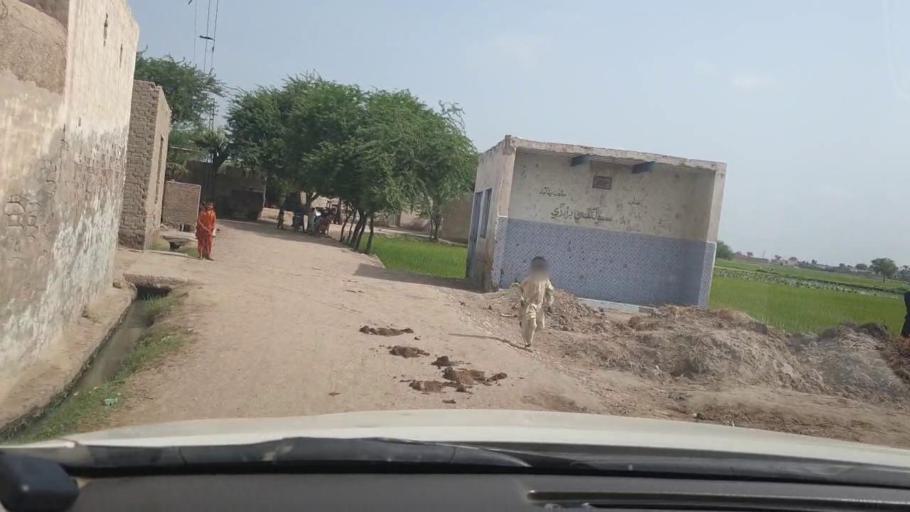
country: PK
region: Sindh
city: Shikarpur
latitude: 28.0078
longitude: 68.5924
